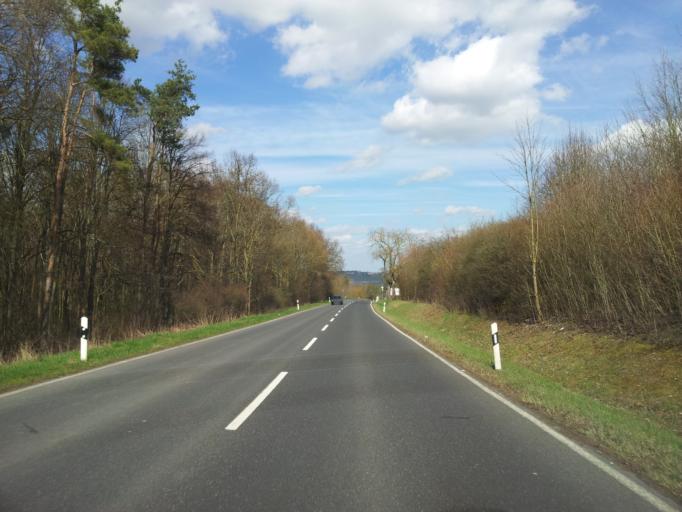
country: DE
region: Bavaria
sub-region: Regierungsbezirk Unterfranken
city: Reichenberg
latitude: 49.7412
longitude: 9.9329
